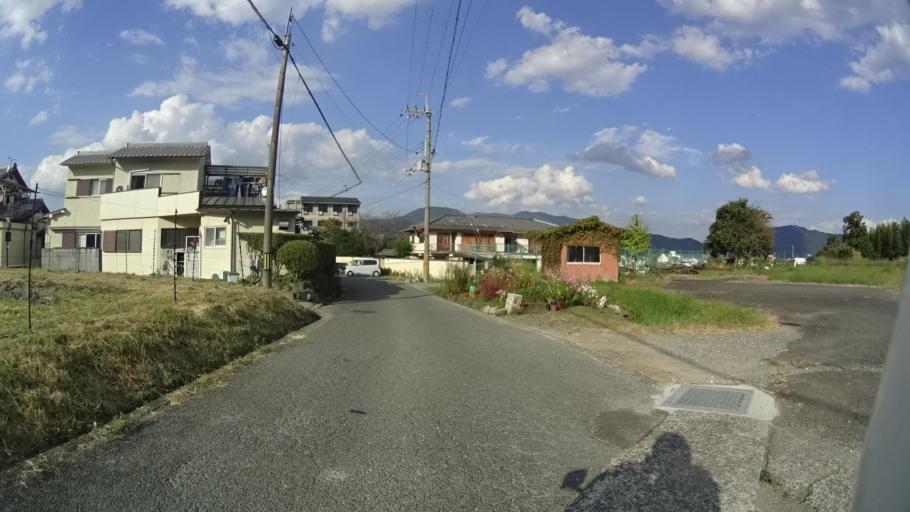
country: JP
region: Kyoto
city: Kameoka
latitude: 35.0061
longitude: 135.5750
